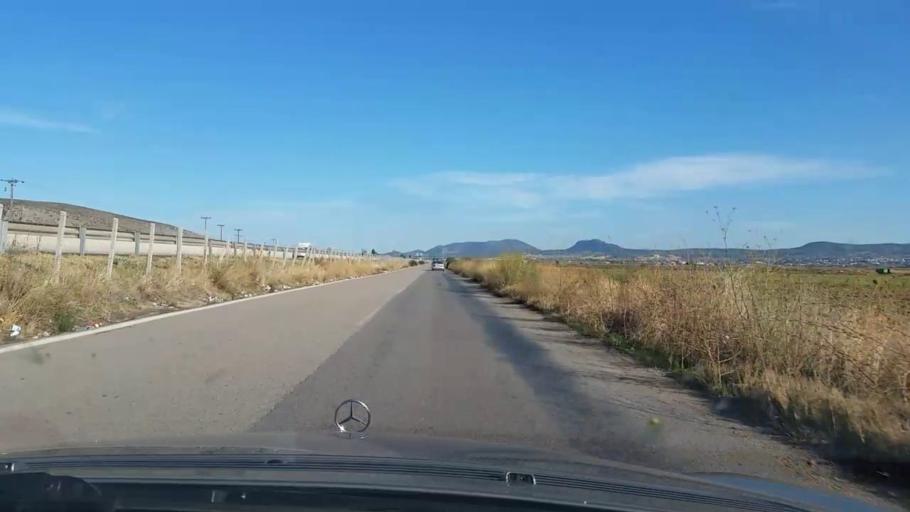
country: GR
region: Central Greece
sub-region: Nomos Voiotias
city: Thivai
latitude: 38.3737
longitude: 23.2739
